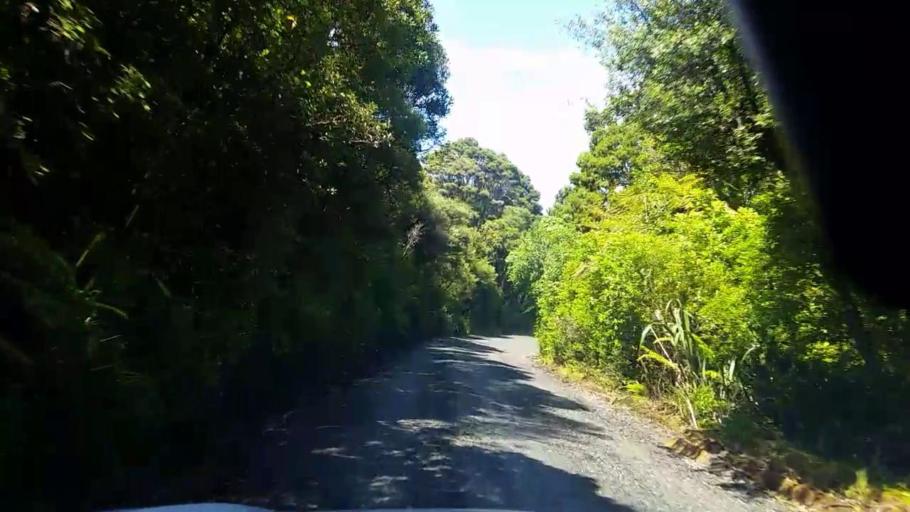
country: NZ
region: Auckland
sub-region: Auckland
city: Titirangi
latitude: -36.9360
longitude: 174.5190
